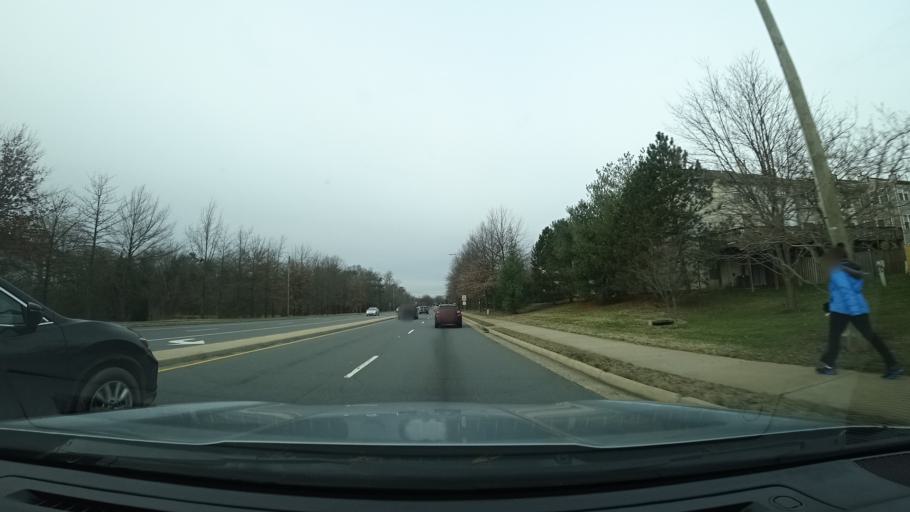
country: US
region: Virginia
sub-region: Fairfax County
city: Floris
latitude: 38.9437
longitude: -77.4020
